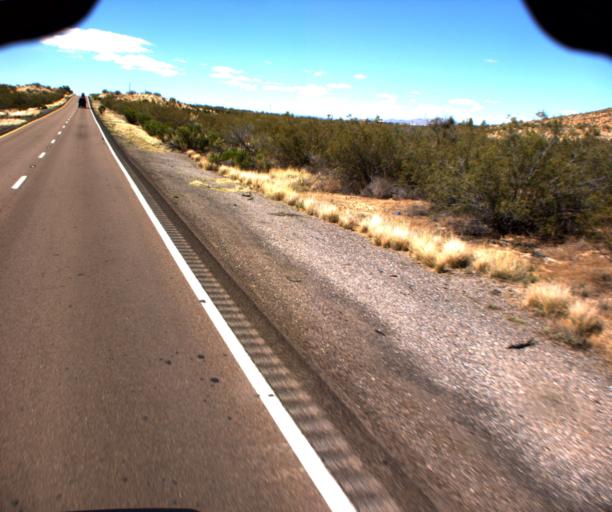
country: US
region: Arizona
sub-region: Mohave County
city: Kingman
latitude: 35.0227
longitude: -113.6641
